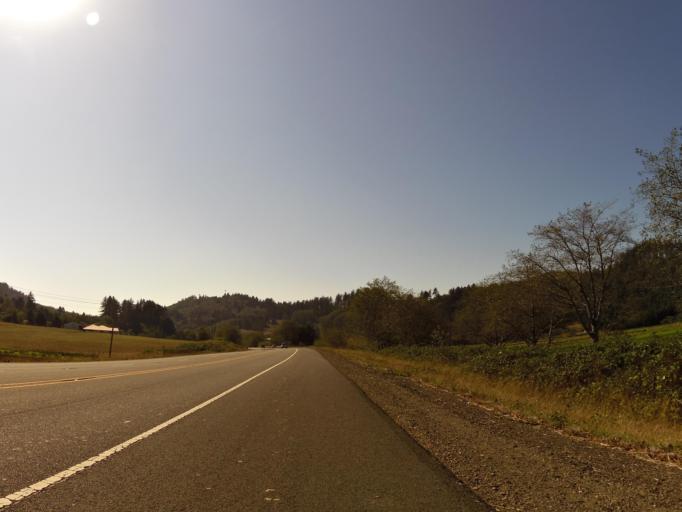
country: US
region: Oregon
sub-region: Tillamook County
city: Pacific City
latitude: 45.1594
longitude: -123.9456
